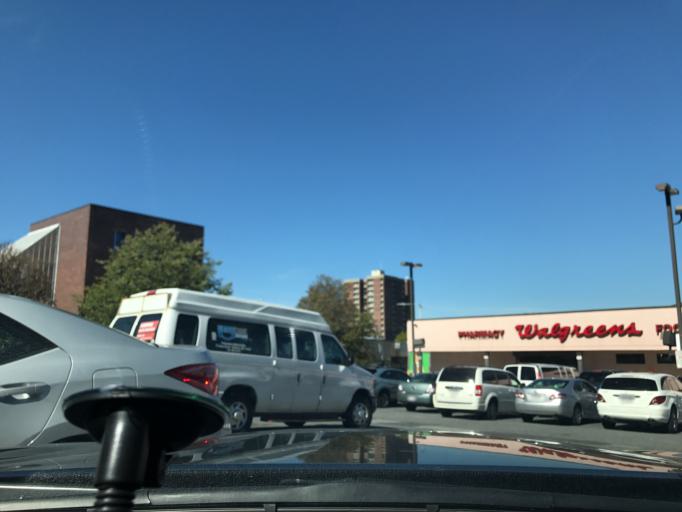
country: US
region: Massachusetts
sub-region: Suffolk County
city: South Boston
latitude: 42.3163
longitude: -71.0824
